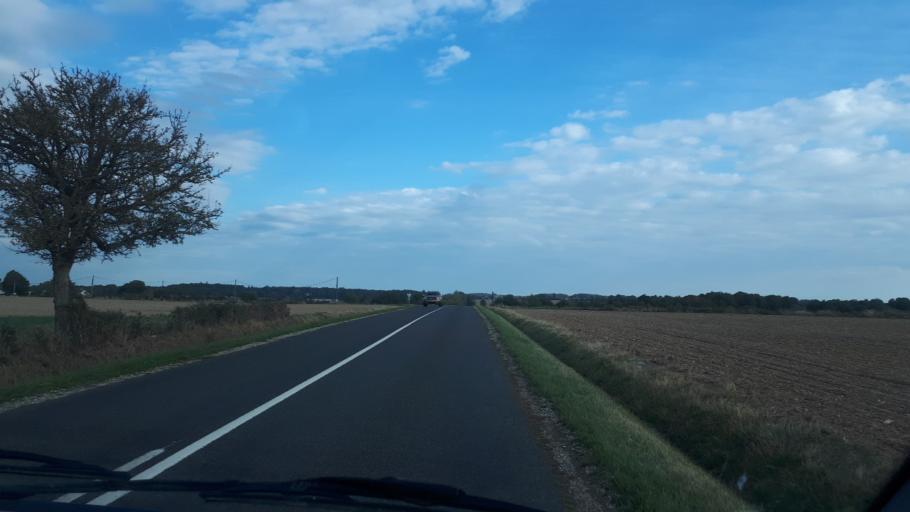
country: FR
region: Centre
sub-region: Departement du Loir-et-Cher
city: Mondoubleau
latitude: 47.9134
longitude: 0.9313
